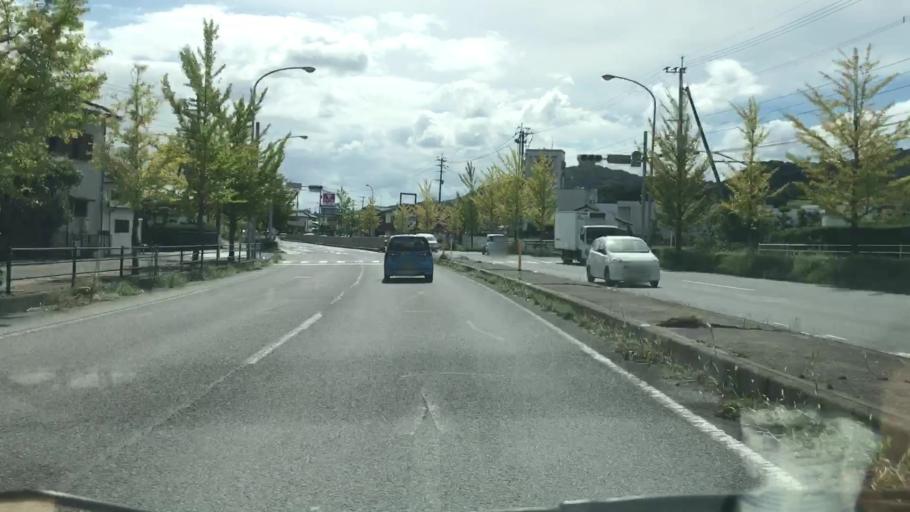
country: JP
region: Saga Prefecture
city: Saga-shi
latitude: 33.2434
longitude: 130.1863
